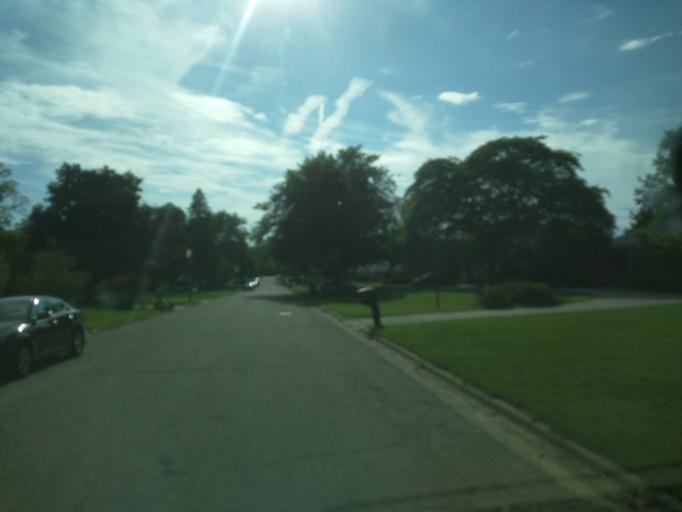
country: US
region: Michigan
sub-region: Ingham County
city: Edgemont Park
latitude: 42.7494
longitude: -84.6089
